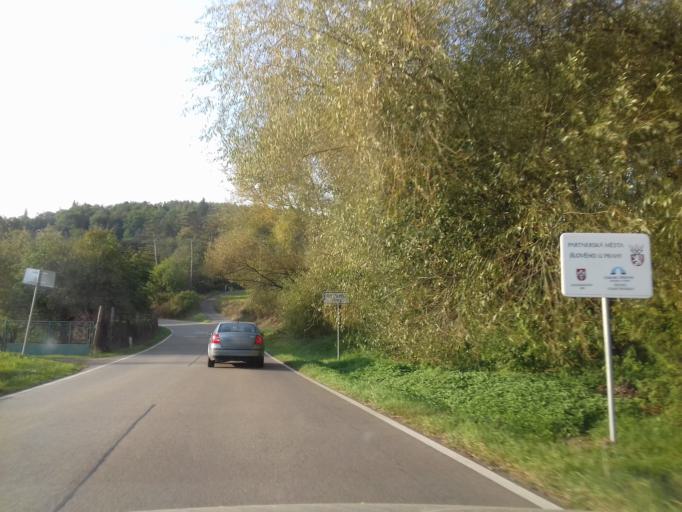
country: CZ
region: Central Bohemia
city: Kamenny Privoz
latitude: 49.8727
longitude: 14.5028
